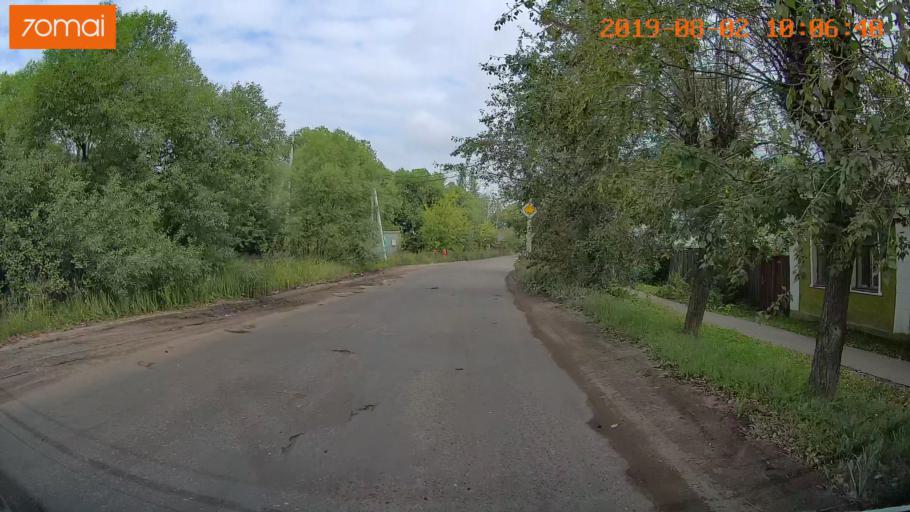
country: RU
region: Ivanovo
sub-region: Gorod Ivanovo
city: Ivanovo
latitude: 56.9799
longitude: 40.9351
